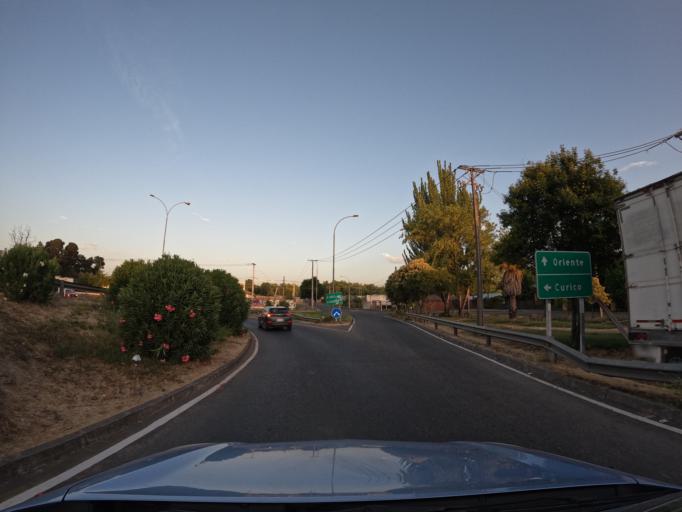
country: CL
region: Maule
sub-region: Provincia de Curico
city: Curico
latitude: -34.9966
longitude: -71.2334
